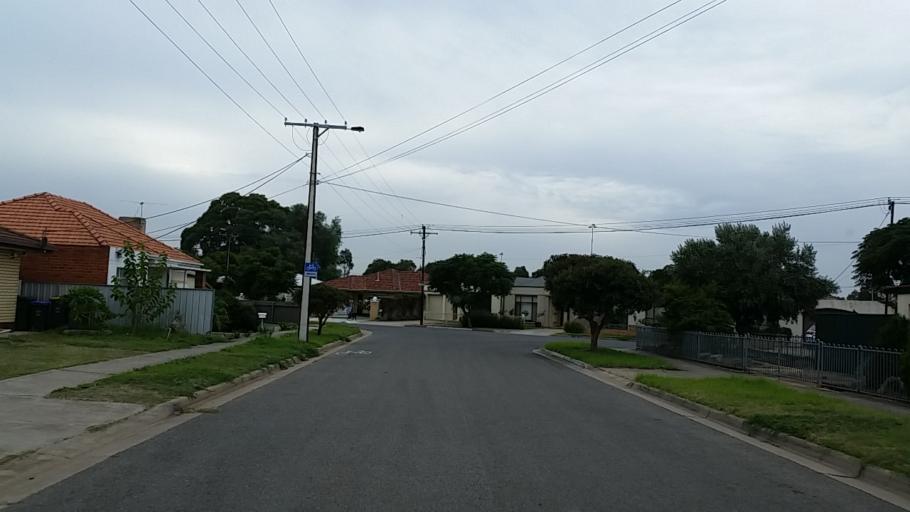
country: AU
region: South Australia
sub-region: Charles Sturt
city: Royal Park
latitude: -34.8752
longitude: 138.5063
